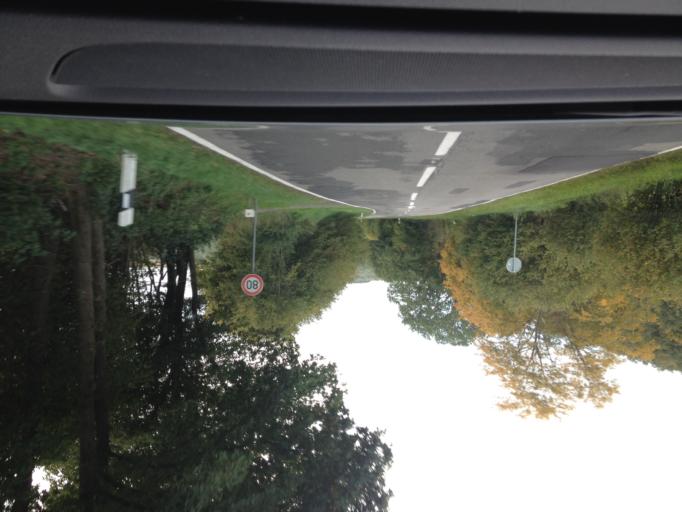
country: DE
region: Saarland
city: Sankt Wendel
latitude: 49.4968
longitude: 7.2207
